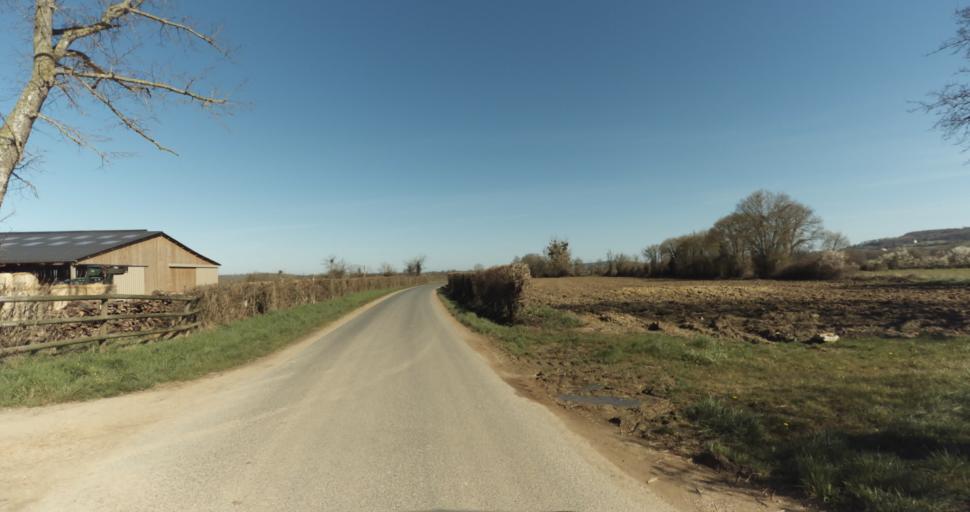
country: FR
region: Lower Normandy
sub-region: Departement de l'Orne
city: Trun
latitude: 48.9208
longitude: 0.0288
